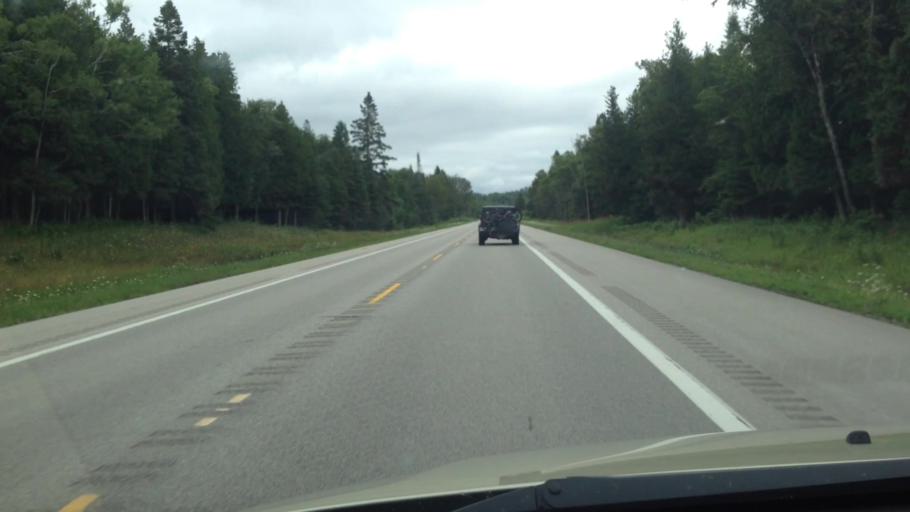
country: US
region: Michigan
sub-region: Luce County
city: Newberry
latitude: 46.0683
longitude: -85.2227
